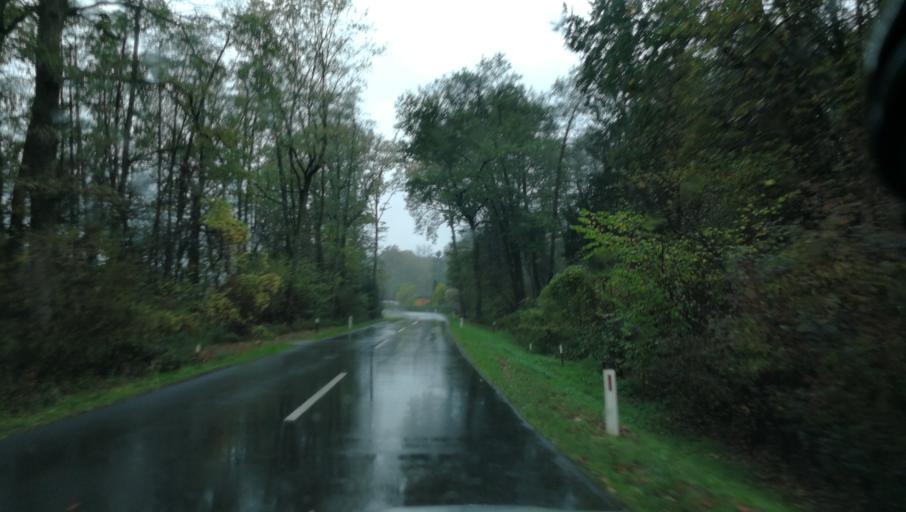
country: AT
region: Styria
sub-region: Politischer Bezirk Leibnitz
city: Spielfeld
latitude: 46.7327
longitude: 15.6722
